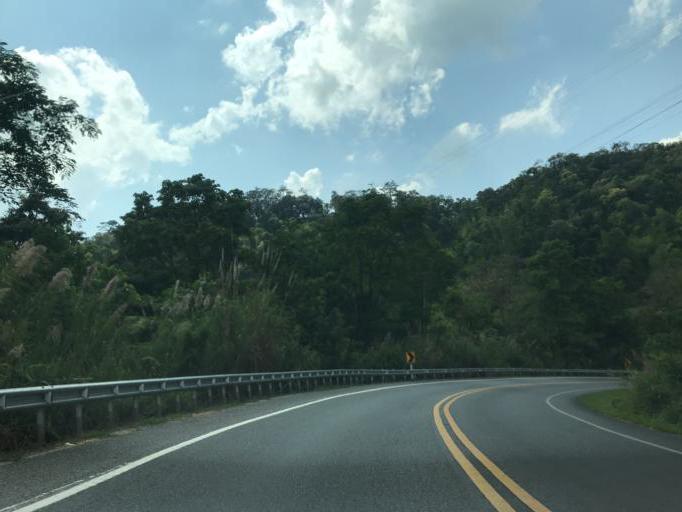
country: TH
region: Phayao
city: Phayao
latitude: 19.0702
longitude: 99.7682
